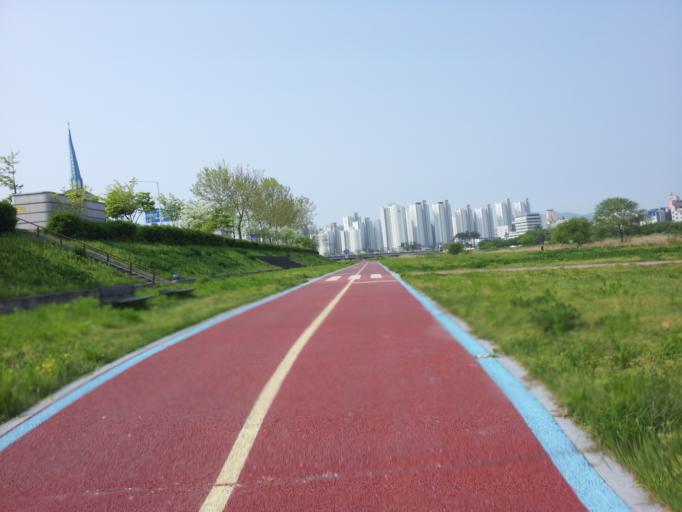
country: KR
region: Daejeon
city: Daejeon
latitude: 36.3548
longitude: 127.3541
